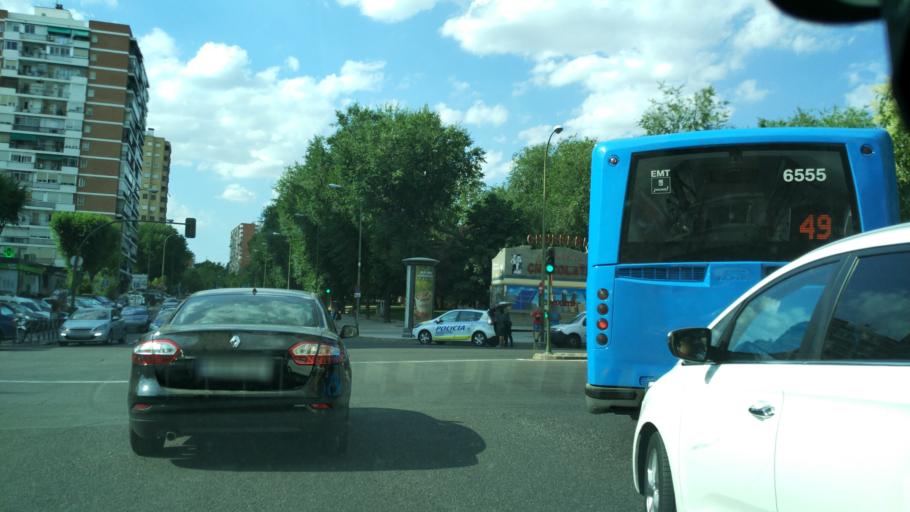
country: ES
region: Madrid
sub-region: Provincia de Madrid
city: Tetuan de las Victorias
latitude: 40.4774
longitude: -3.7120
